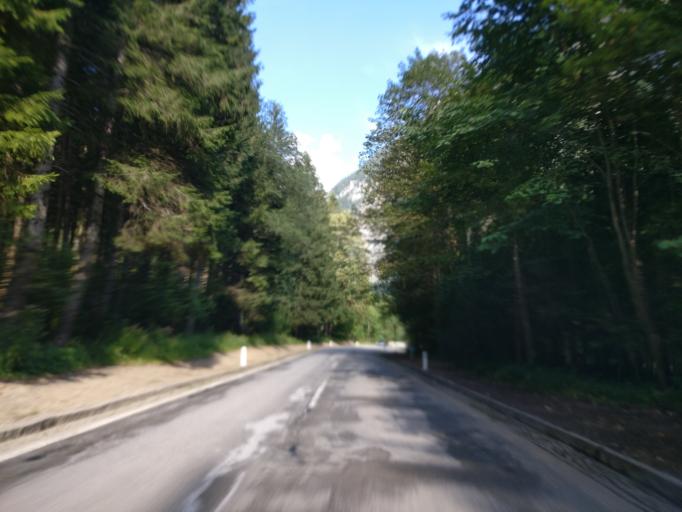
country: AT
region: Styria
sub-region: Politischer Bezirk Leoben
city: Hieflau
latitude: 47.5883
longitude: 14.6662
